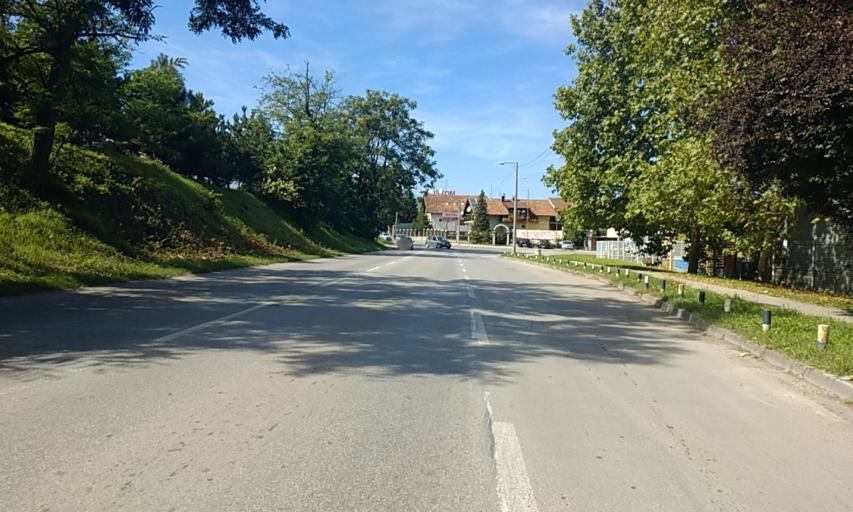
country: BA
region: Republika Srpska
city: Banja Luka
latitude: 44.7892
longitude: 17.2028
